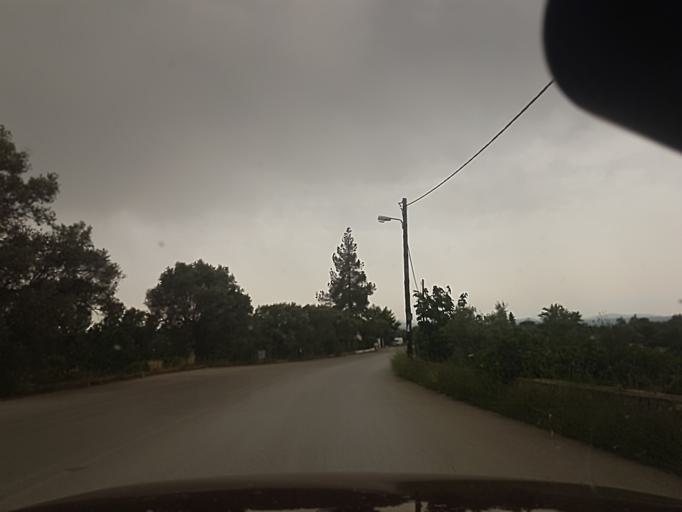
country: GR
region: Central Greece
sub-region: Nomos Evvoias
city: Filla
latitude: 38.4416
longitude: 23.6726
